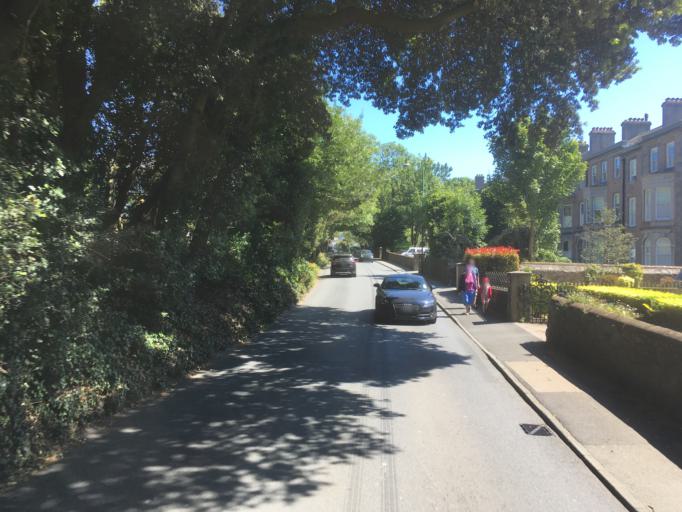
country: GG
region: St Peter Port
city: Saint Peter Port
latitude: 49.4579
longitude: -2.5526
